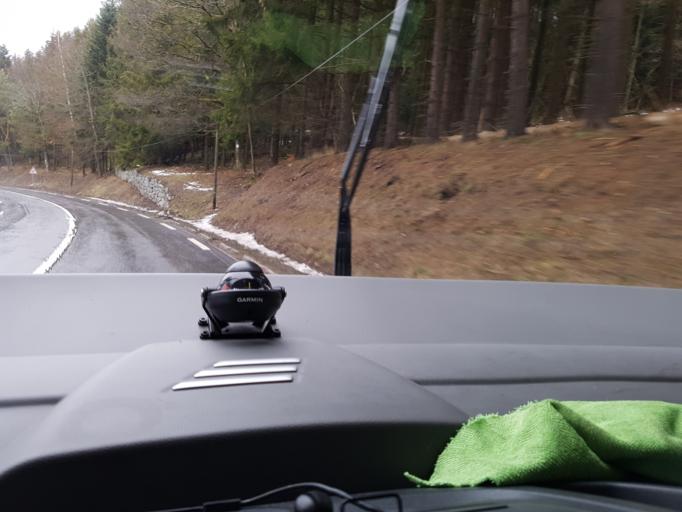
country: FR
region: Lorraine
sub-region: Departement des Vosges
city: Plainfaing
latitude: 48.1783
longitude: 7.0261
